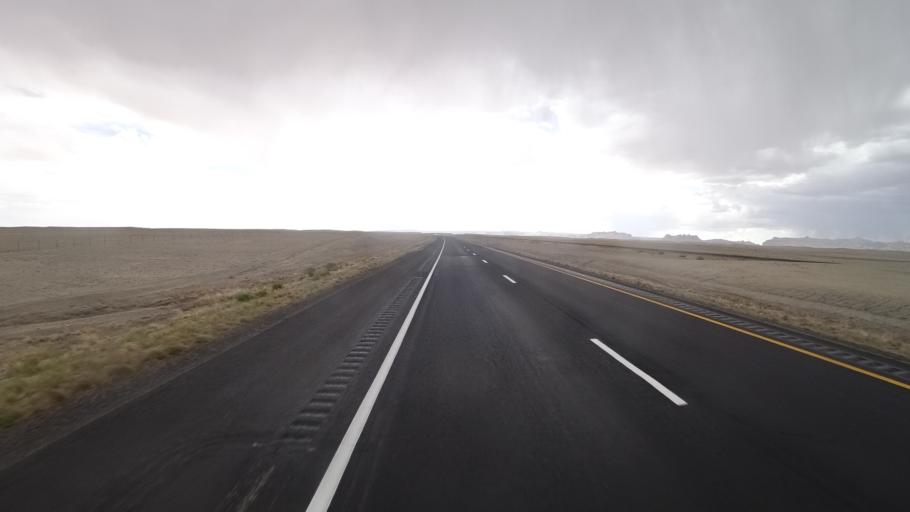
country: US
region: Utah
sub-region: Carbon County
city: East Carbon City
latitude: 38.9502
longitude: -110.3160
